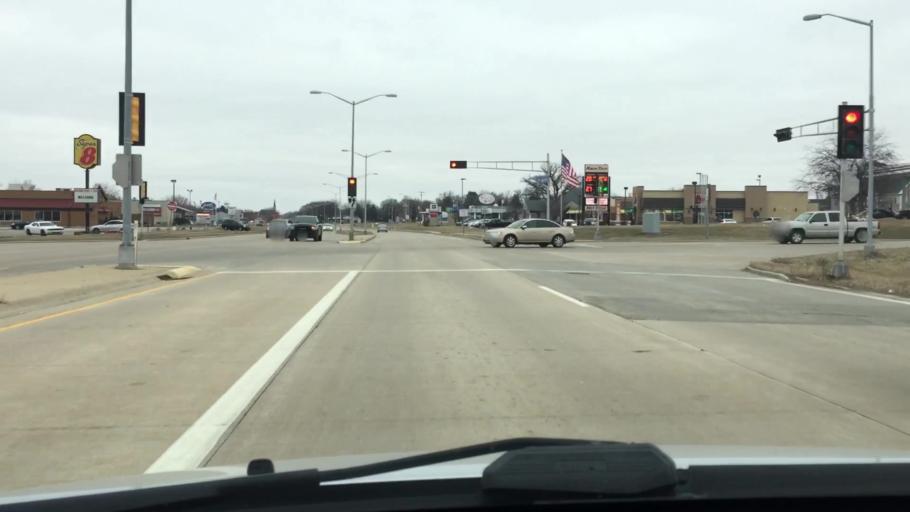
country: US
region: Wisconsin
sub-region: Jefferson County
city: Watertown
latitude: 43.1697
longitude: -88.7329
